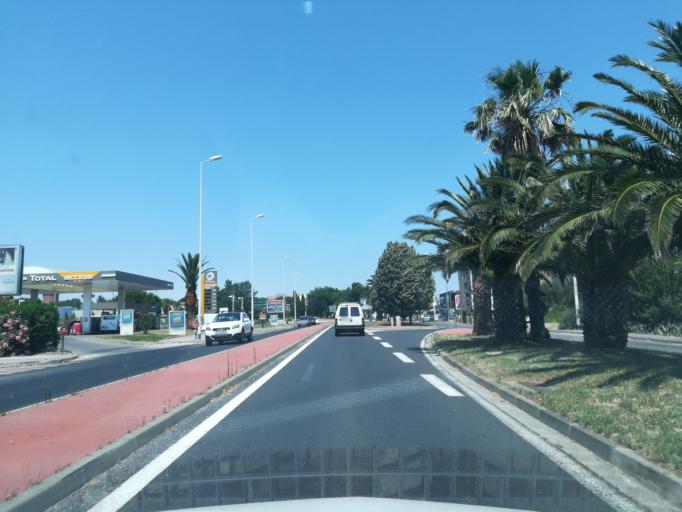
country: FR
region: Languedoc-Roussillon
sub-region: Departement des Pyrenees-Orientales
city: Perpignan
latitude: 42.6772
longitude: 2.8906
